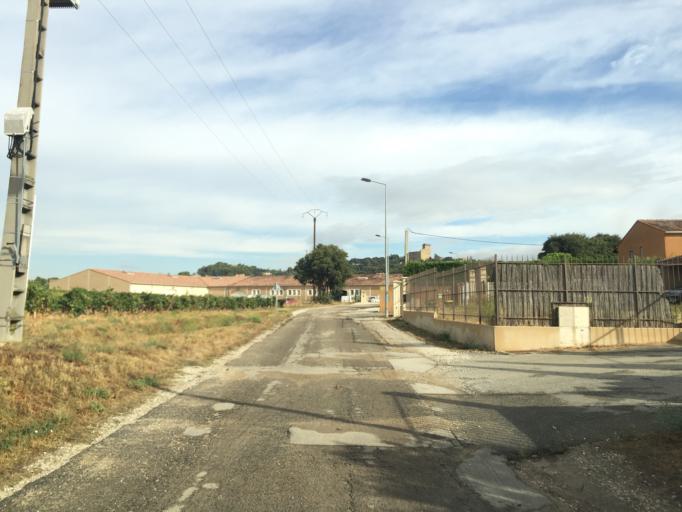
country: FR
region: Provence-Alpes-Cote d'Azur
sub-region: Departement du Vaucluse
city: Chateauneuf-du-Pape
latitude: 44.0487
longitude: 4.8306
